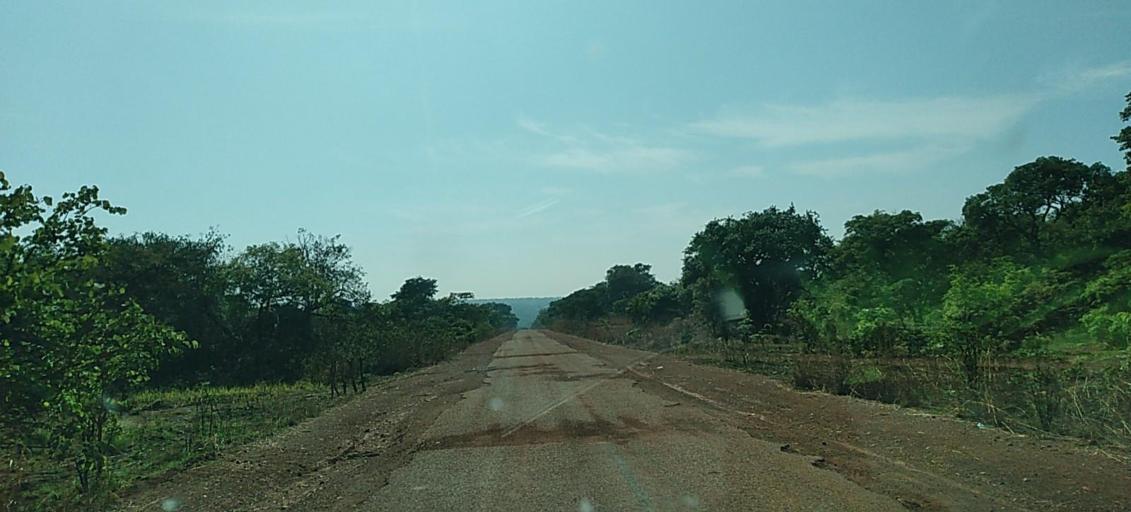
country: ZM
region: North-Western
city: Mwinilunga
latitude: -11.8225
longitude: 25.1090
